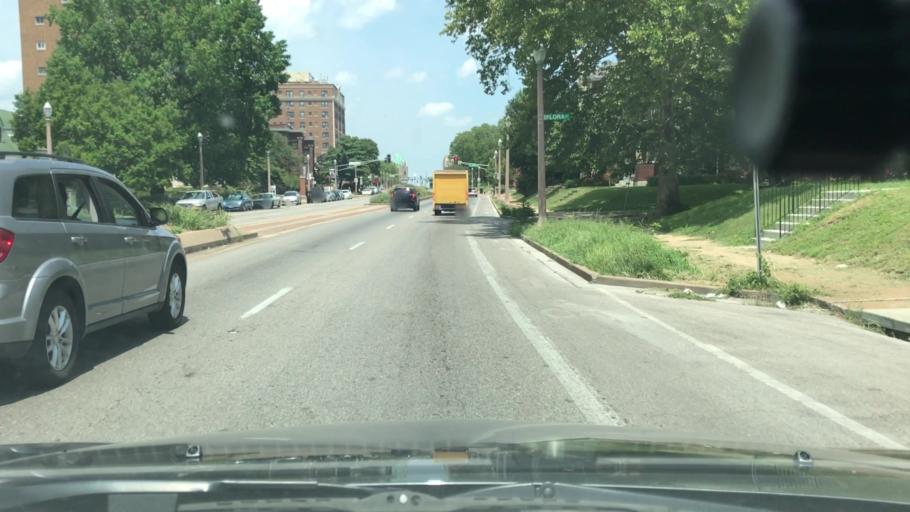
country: US
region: Missouri
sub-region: City of Saint Louis
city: St. Louis
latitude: 38.6121
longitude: -90.2403
